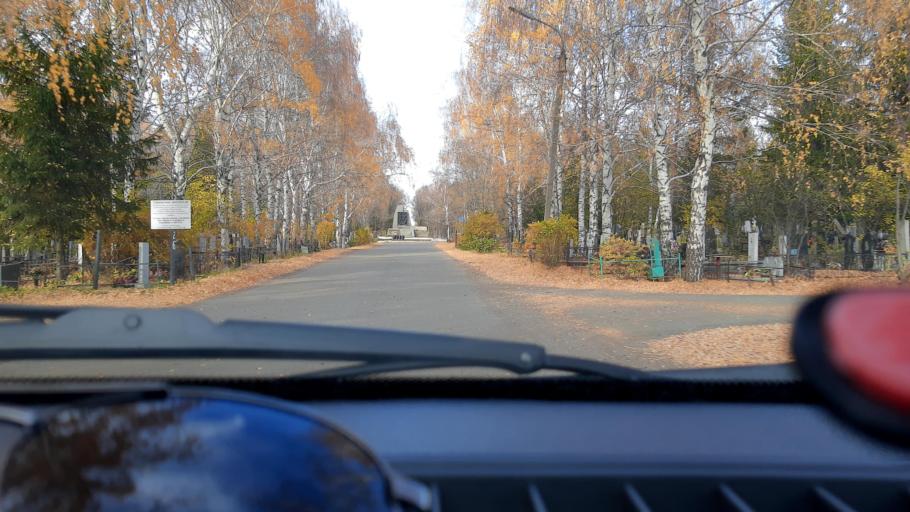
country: RU
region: Bashkortostan
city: Ufa
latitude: 54.8515
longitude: 56.1553
